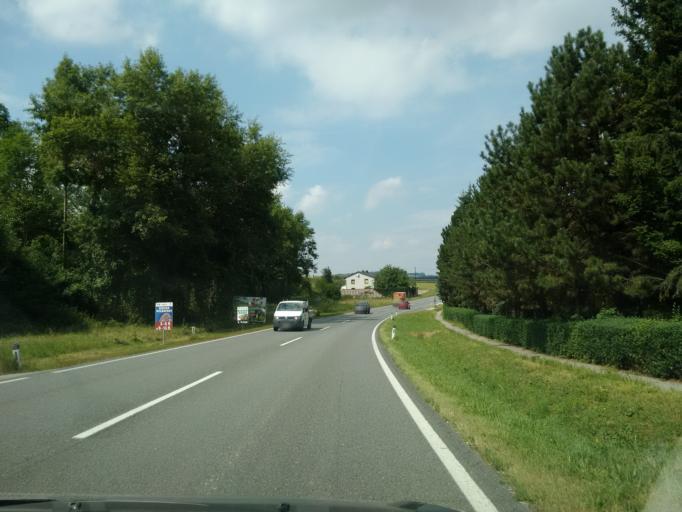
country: AT
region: Upper Austria
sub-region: Wels-Land
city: Buchkirchen
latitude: 48.2127
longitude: 13.9732
